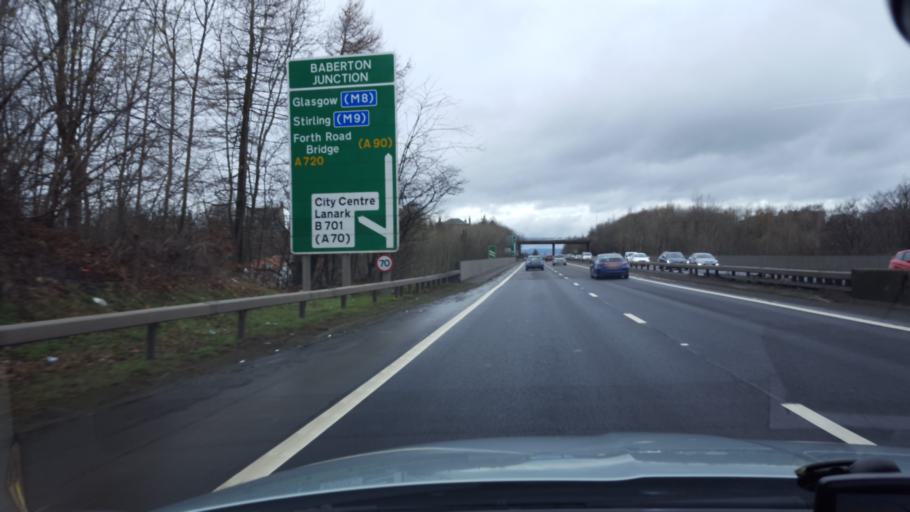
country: GB
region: Scotland
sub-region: Edinburgh
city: Colinton
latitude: 55.9048
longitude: -3.2750
